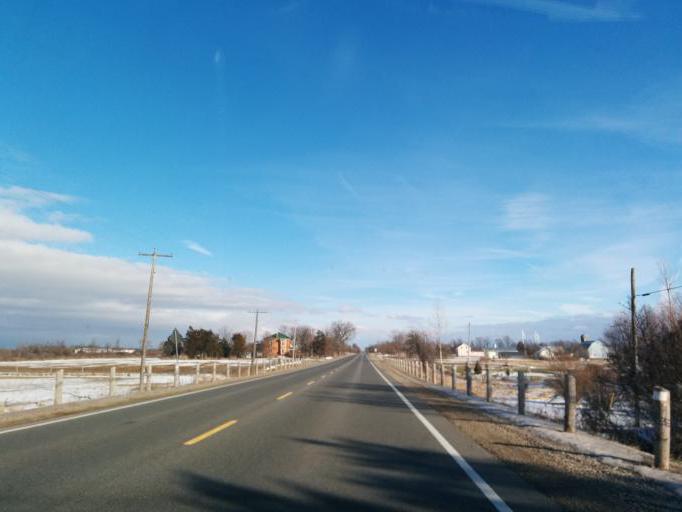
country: CA
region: Ontario
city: Ancaster
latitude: 42.9311
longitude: -79.9368
